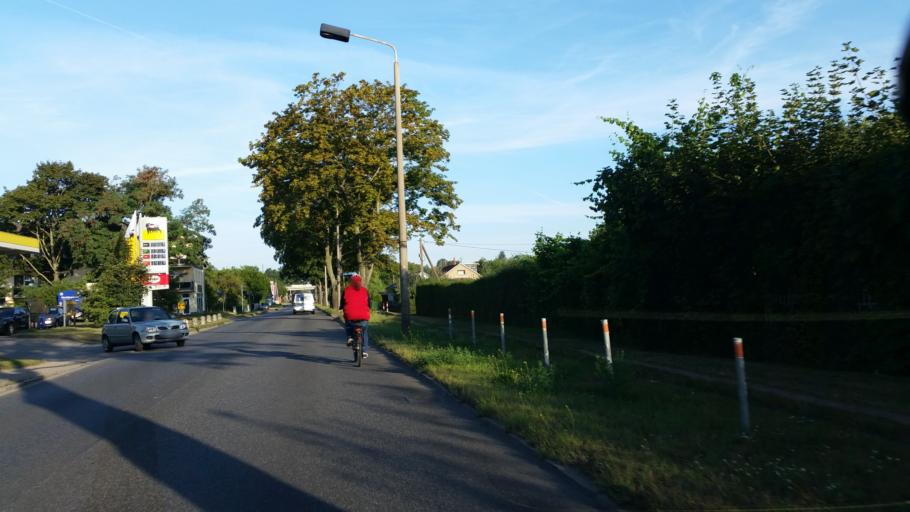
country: DE
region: Brandenburg
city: Grossbeeren
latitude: 52.3872
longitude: 13.3052
